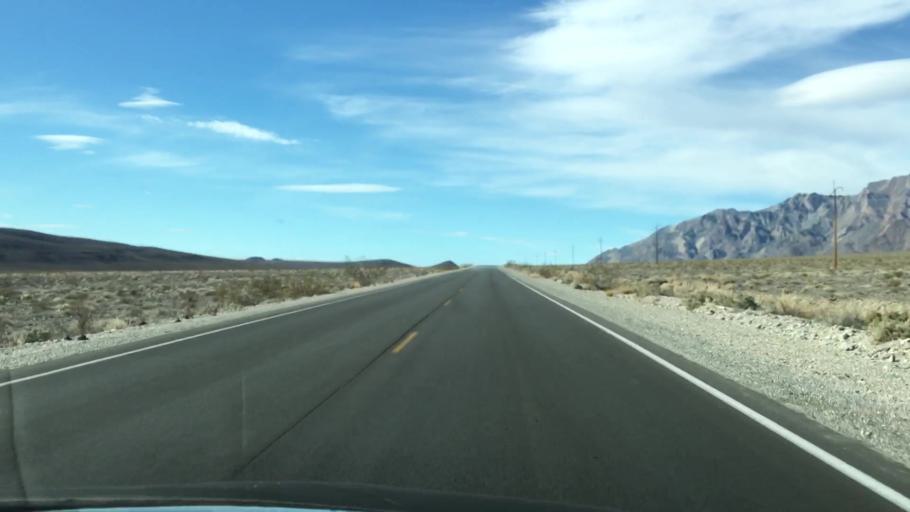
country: US
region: Nevada
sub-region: Nye County
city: Pahrump
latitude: 36.3213
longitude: -116.5550
